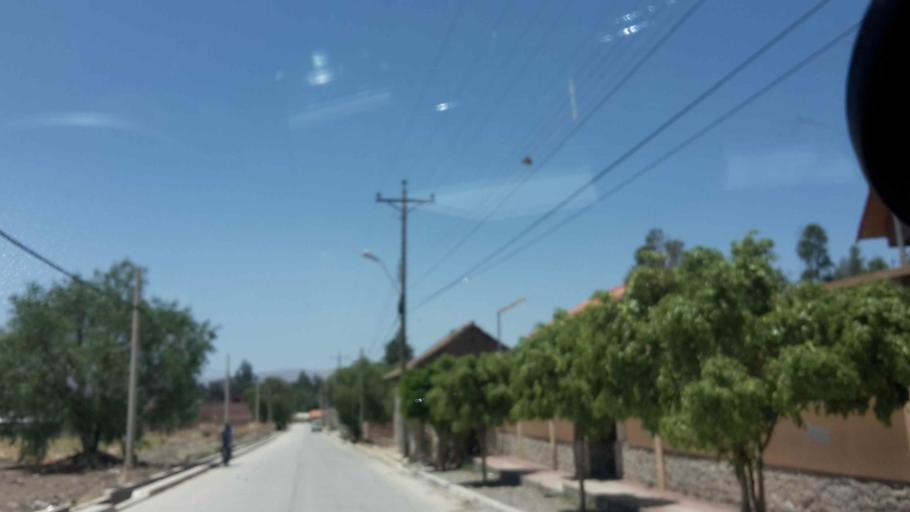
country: BO
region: Cochabamba
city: Cochabamba
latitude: -17.3533
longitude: -66.2069
